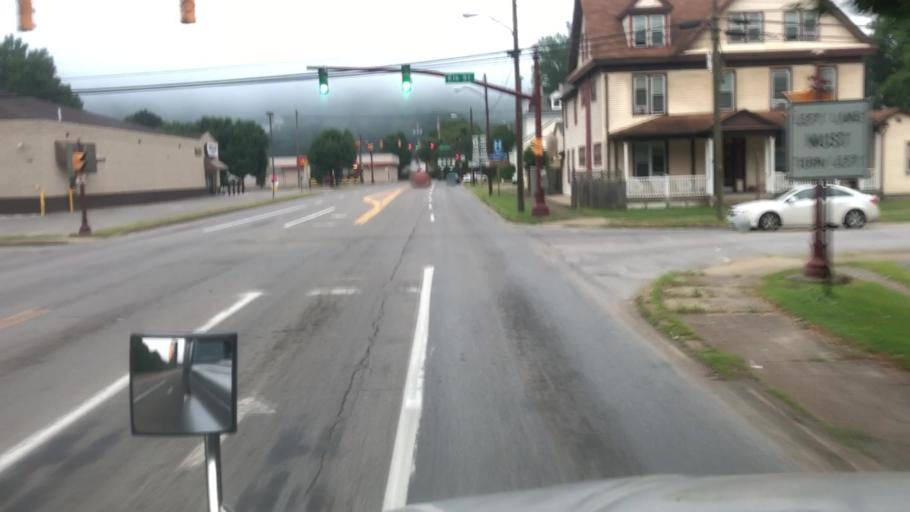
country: US
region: Pennsylvania
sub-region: Venango County
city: Franklin
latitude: 41.3945
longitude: -79.8244
